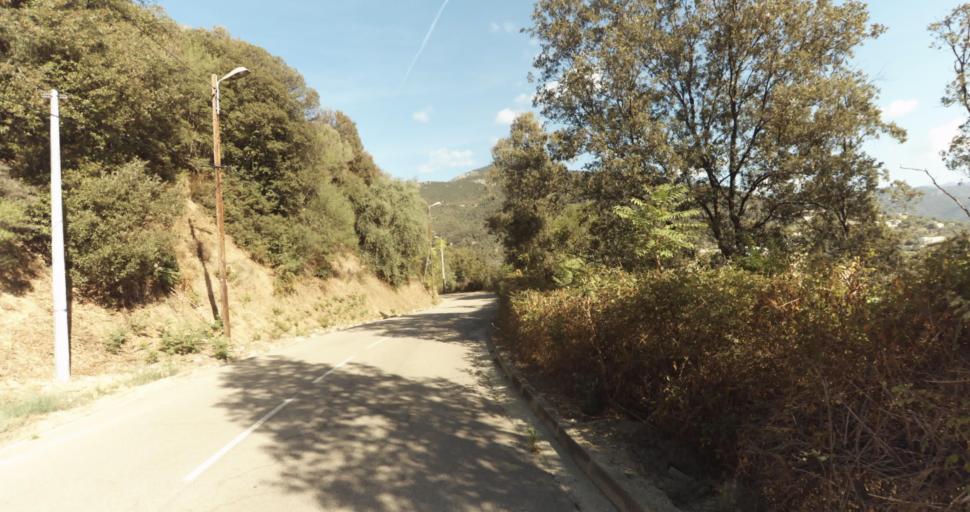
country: FR
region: Corsica
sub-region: Departement de la Corse-du-Sud
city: Ajaccio
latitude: 41.9254
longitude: 8.7086
